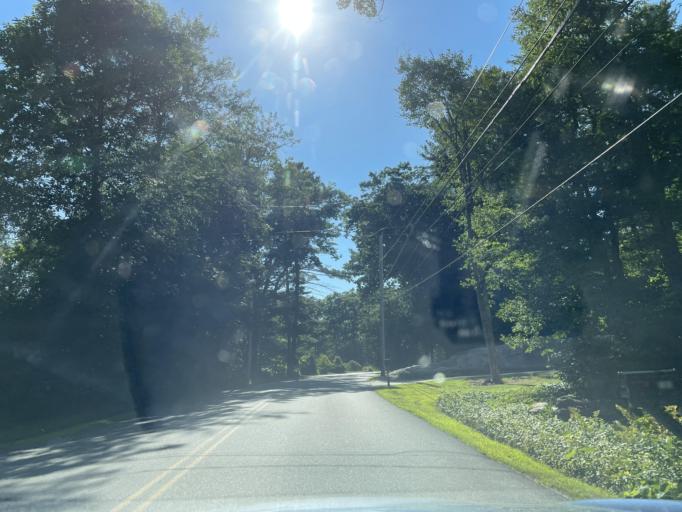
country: US
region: Massachusetts
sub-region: Worcester County
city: Charlton
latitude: 42.1609
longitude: -72.0135
